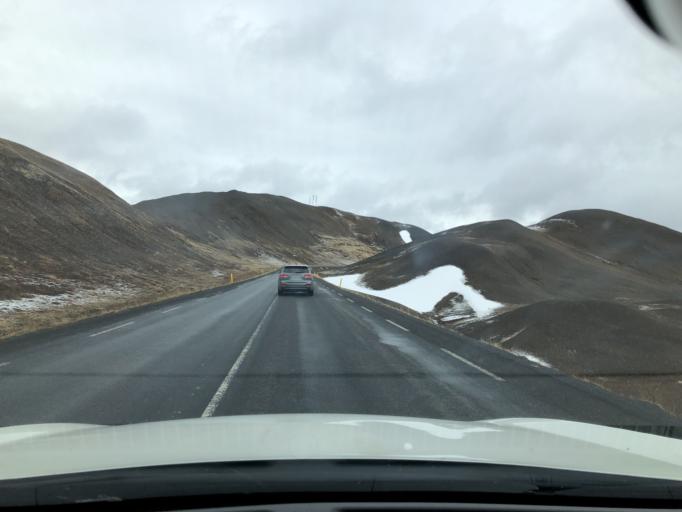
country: IS
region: Northeast
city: Laugar
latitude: 65.6437
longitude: -16.8310
